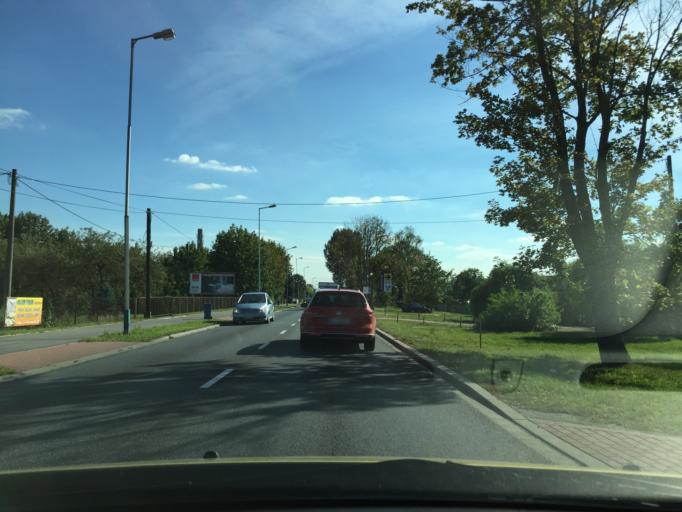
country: PL
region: Greater Poland Voivodeship
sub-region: Kalisz
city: Kalisz
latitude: 51.7869
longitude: 18.0902
